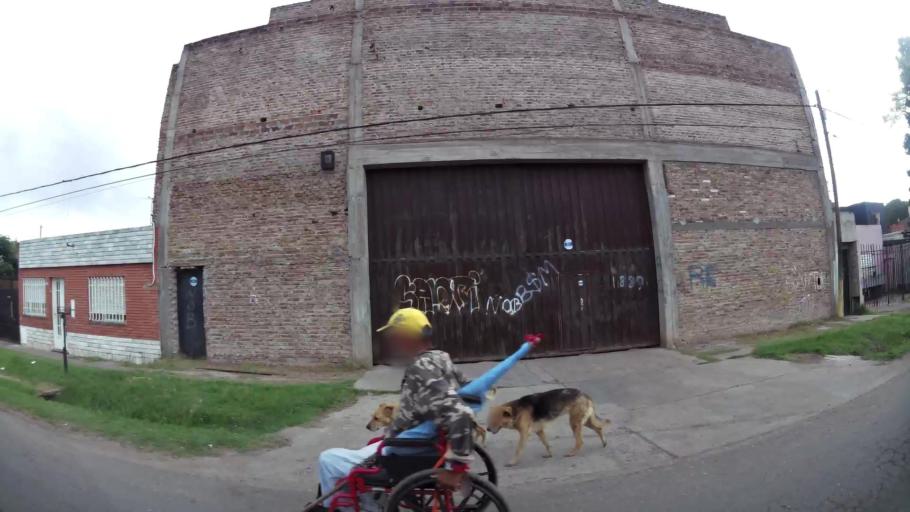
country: AR
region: Santa Fe
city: Gobernador Galvez
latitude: -32.9981
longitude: -60.6798
